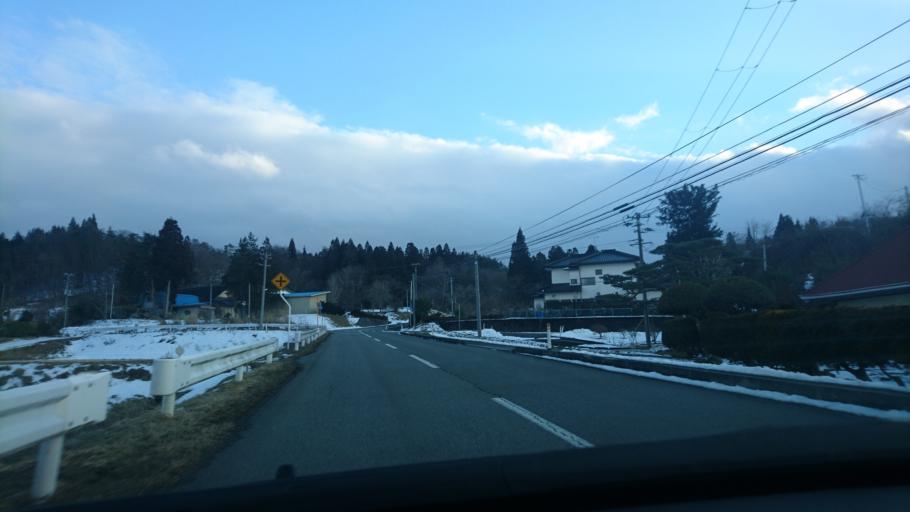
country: JP
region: Iwate
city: Ichinoseki
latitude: 39.0163
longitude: 141.3390
